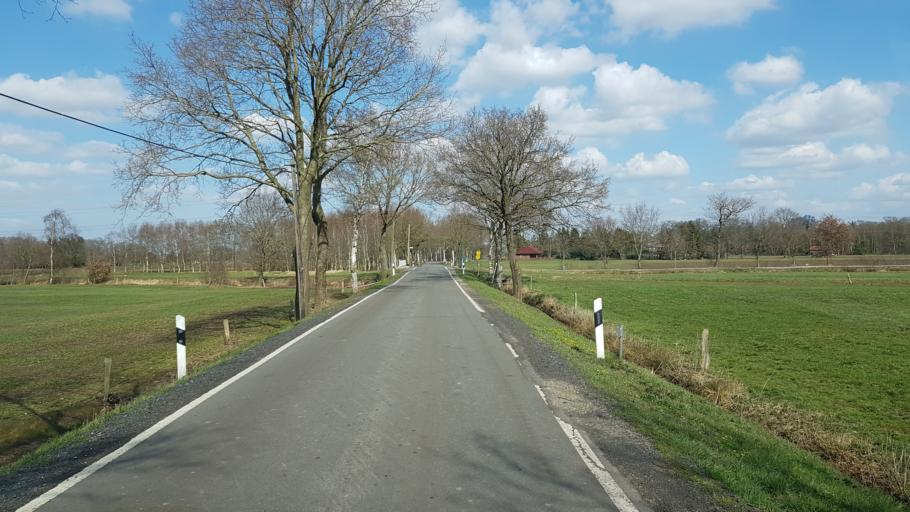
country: DE
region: Lower Saxony
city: Rastede
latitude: 53.2956
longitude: 8.1955
